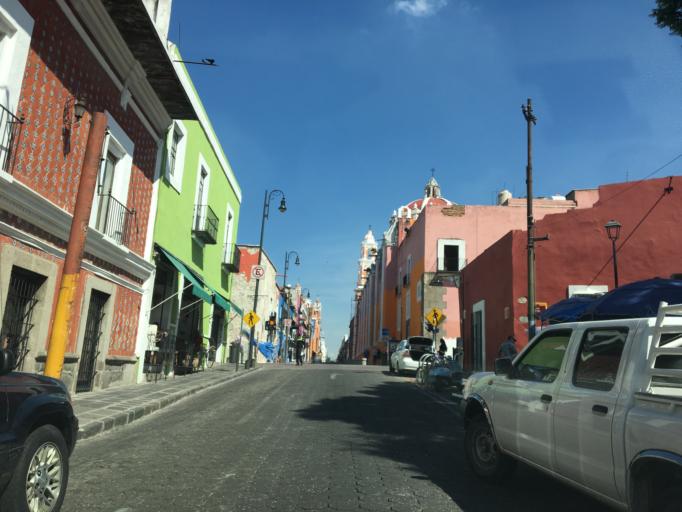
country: MX
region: Puebla
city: Puebla
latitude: 19.0405
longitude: -98.1967
